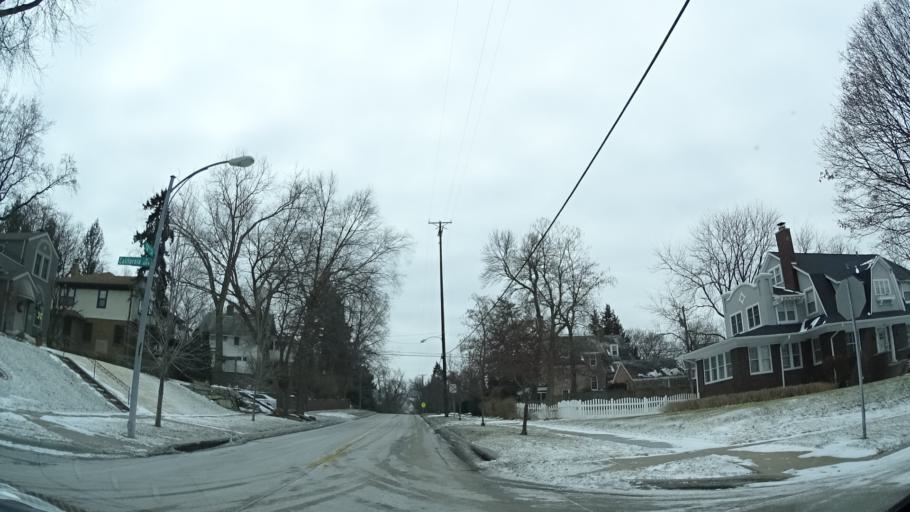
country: US
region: Nebraska
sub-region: Douglas County
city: Omaha
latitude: 41.2642
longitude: -95.9951
